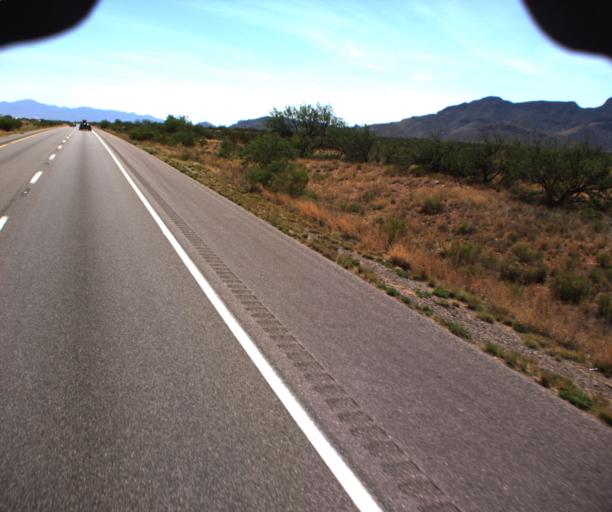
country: US
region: Arizona
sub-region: Cochise County
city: Whetstone
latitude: 31.8270
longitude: -110.3455
